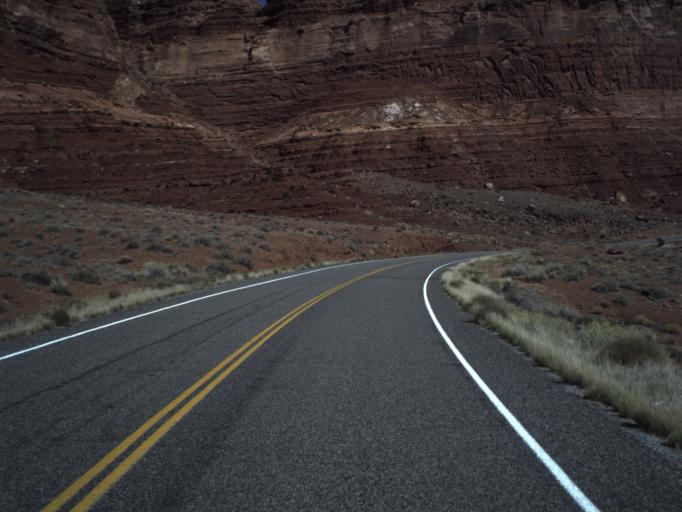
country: US
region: Utah
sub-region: San Juan County
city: Blanding
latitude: 37.9179
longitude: -110.3981
